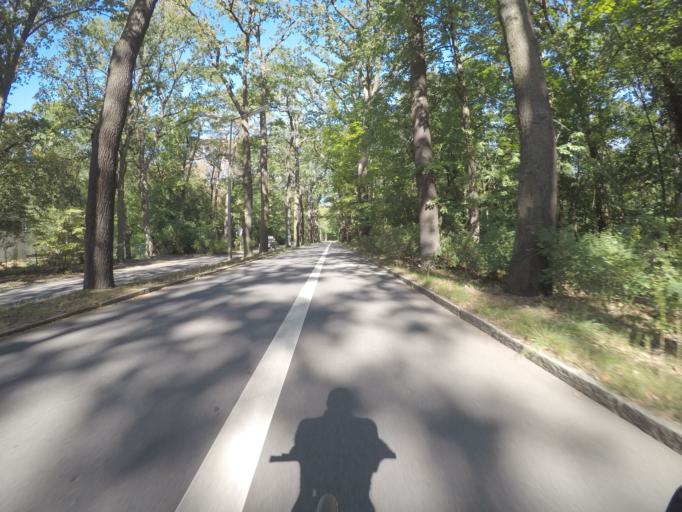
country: DE
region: Berlin
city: Konradshohe
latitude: 52.5773
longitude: 13.2286
